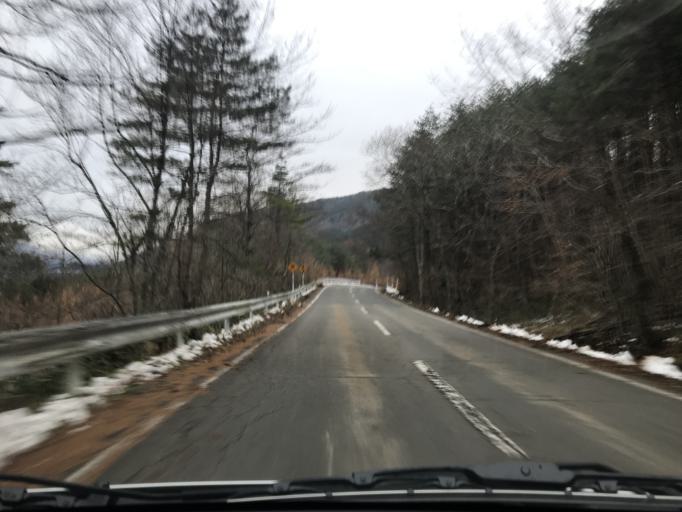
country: JP
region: Iwate
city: Mizusawa
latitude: 39.1485
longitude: 141.3631
